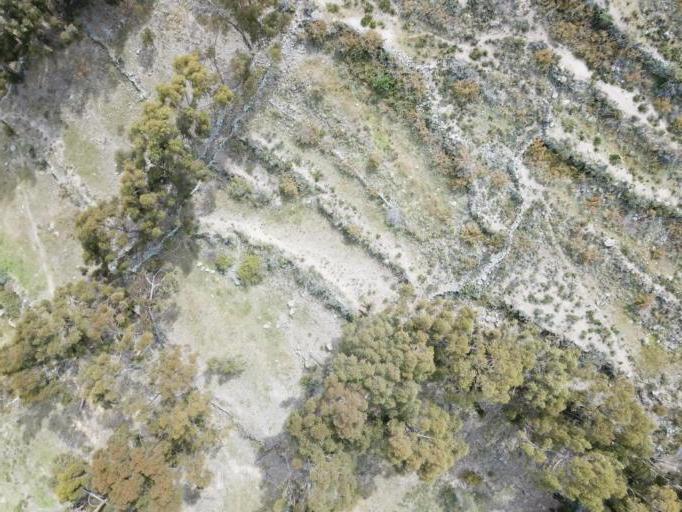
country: BO
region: La Paz
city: Achacachi
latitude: -16.0499
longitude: -68.8177
